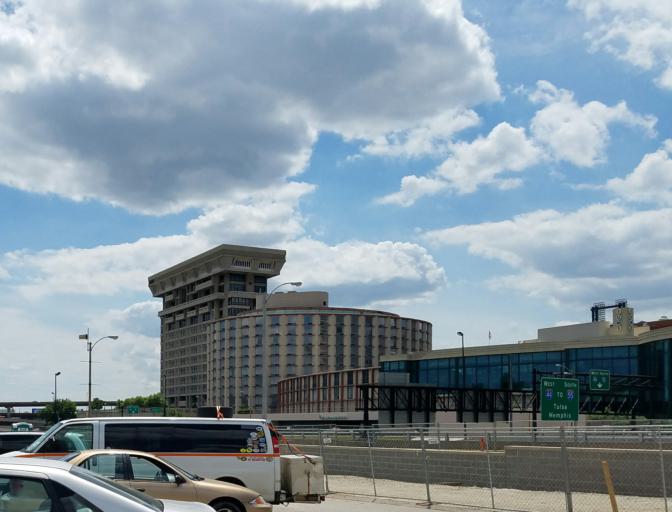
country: US
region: Missouri
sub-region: City of Saint Louis
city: St. Louis
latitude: 38.6241
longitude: -90.1871
